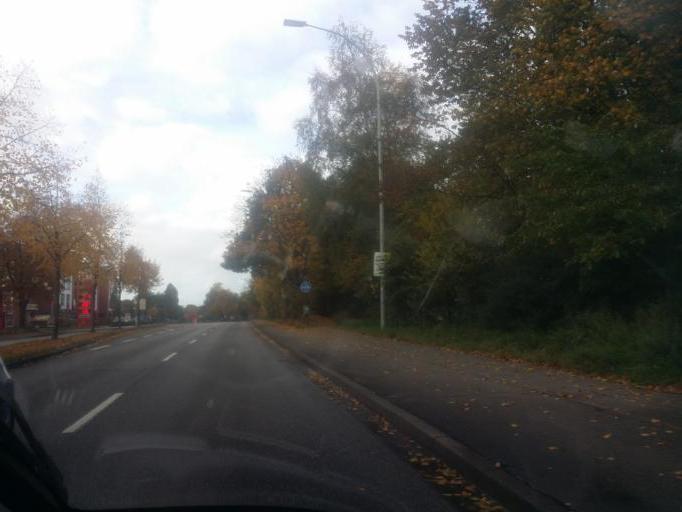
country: DE
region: Schleswig-Holstein
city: Halstenbek
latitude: 53.5991
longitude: 9.8479
